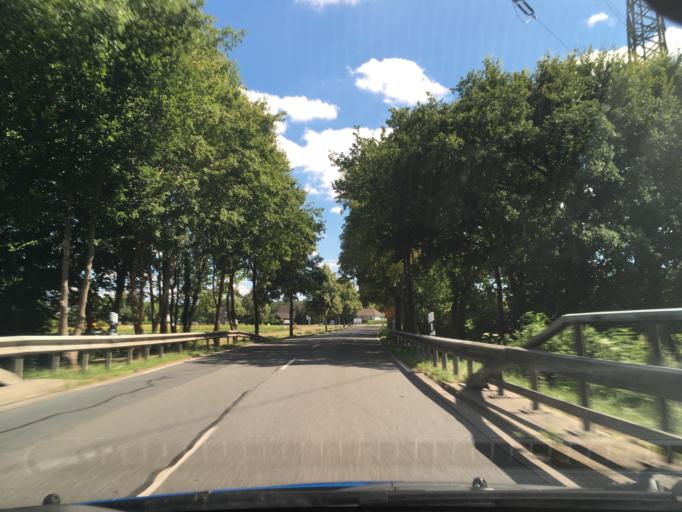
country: DE
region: Lower Saxony
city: Celle
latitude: 52.6254
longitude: 10.1205
